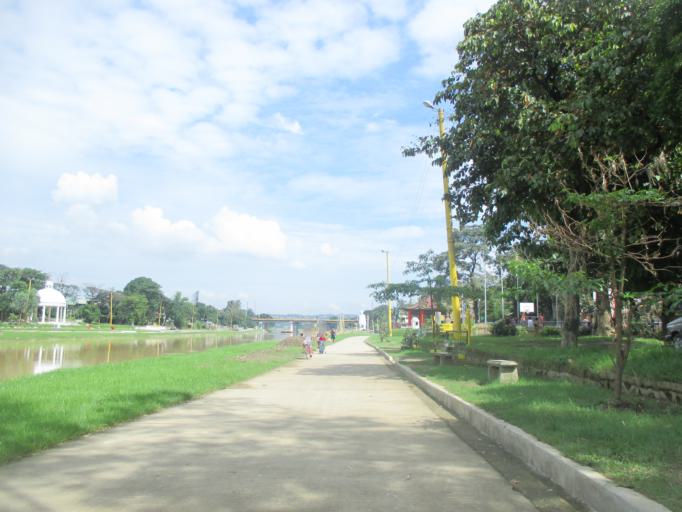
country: PH
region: Metro Manila
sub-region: Marikina
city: Calumpang
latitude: 14.6313
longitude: 121.0942
